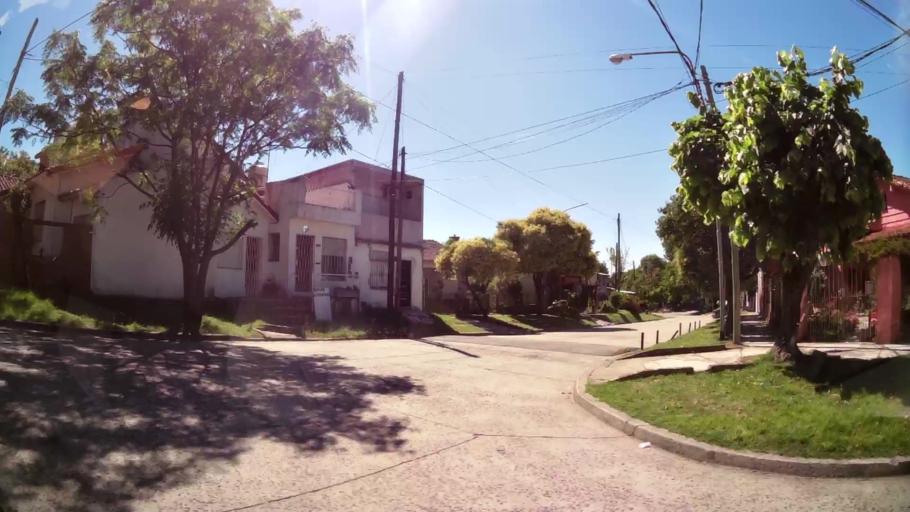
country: AR
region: Buenos Aires
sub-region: Partido de Tigre
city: Tigre
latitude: -34.5032
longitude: -58.6155
